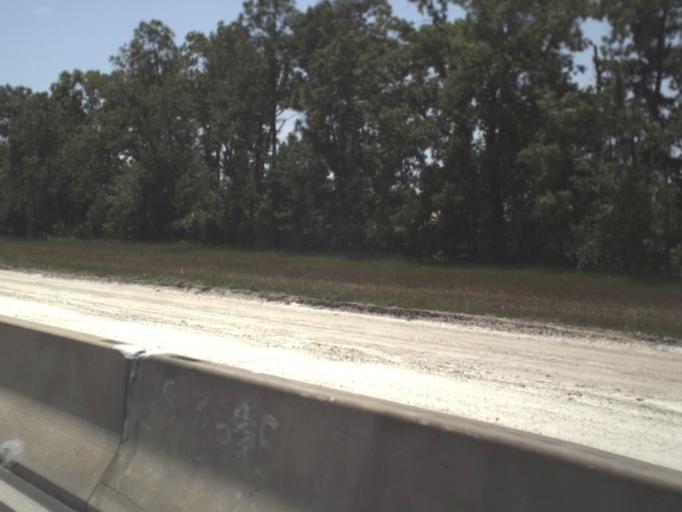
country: US
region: Florida
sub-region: Saint Johns County
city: Fruit Cove
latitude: 30.1217
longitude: -81.5214
